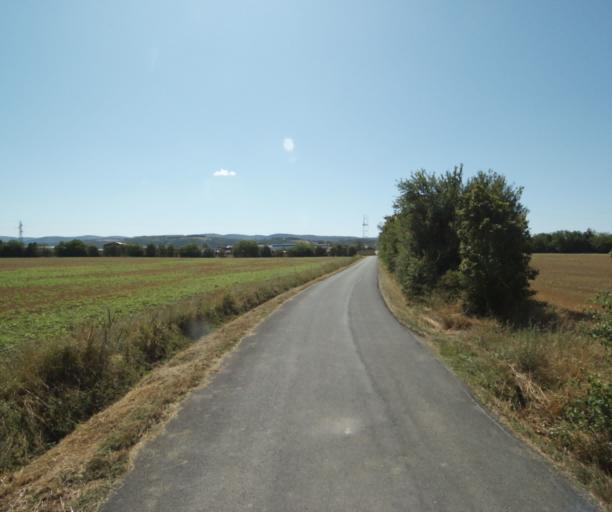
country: FR
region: Midi-Pyrenees
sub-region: Departement de la Haute-Garonne
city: Revel
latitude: 43.4582
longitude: 1.9733
